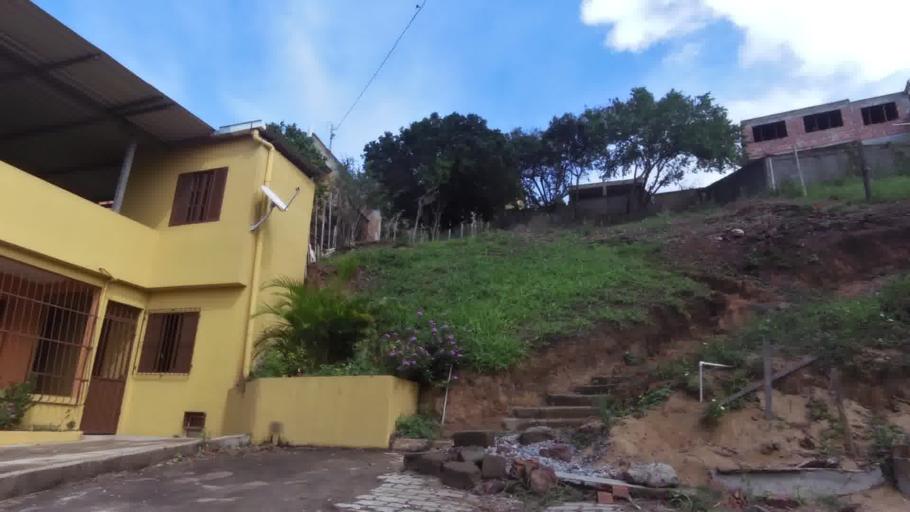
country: BR
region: Espirito Santo
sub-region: Marataizes
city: Marataizes
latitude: -21.0345
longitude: -40.8229
